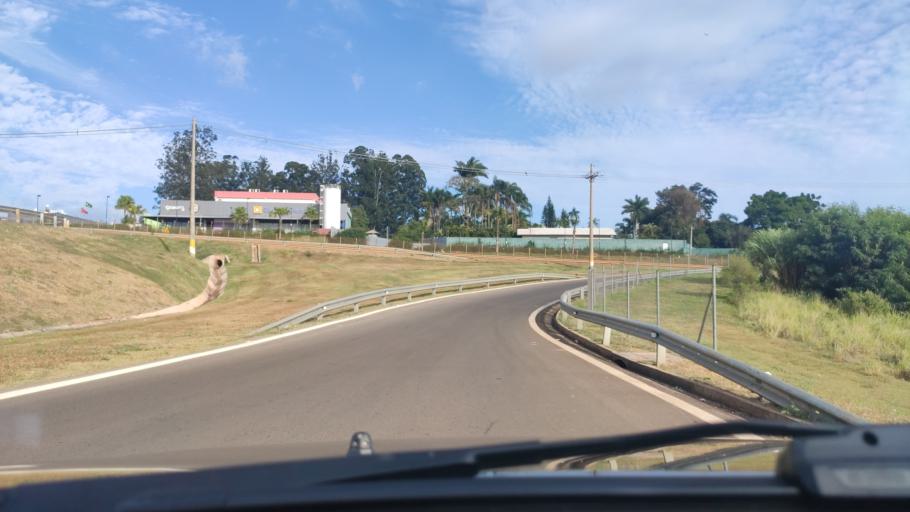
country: BR
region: Sao Paulo
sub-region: Avare
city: Avare
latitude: -23.0950
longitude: -48.9380
